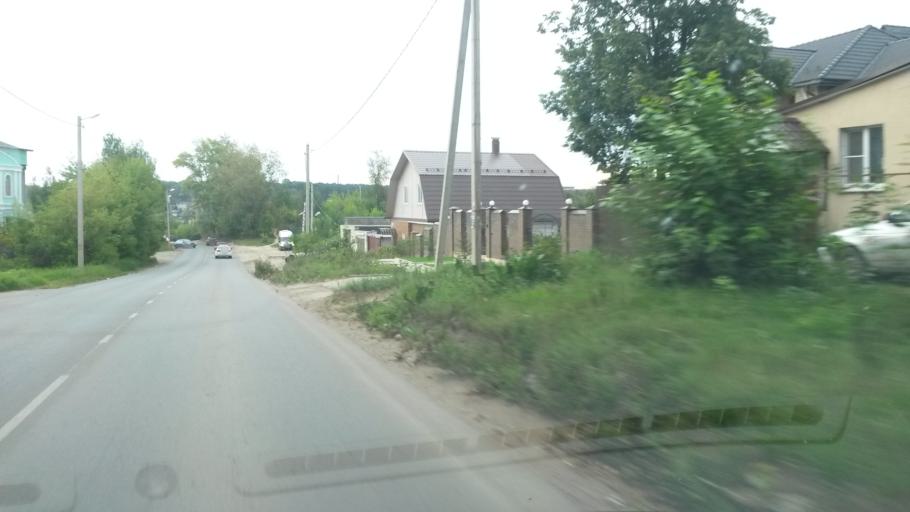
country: RU
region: Ivanovo
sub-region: Gorod Ivanovo
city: Ivanovo
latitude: 57.0300
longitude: 40.9241
